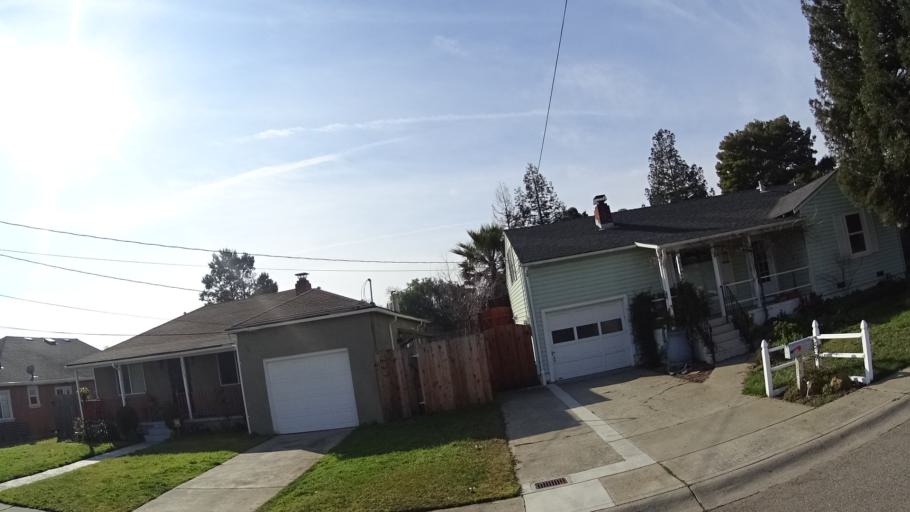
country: US
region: California
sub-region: Alameda County
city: Fairview
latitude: 37.6874
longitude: -122.0524
